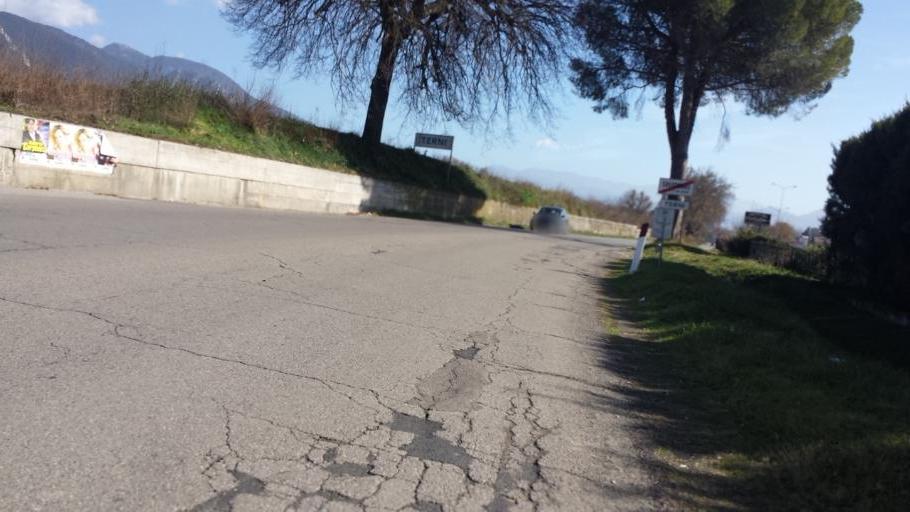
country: IT
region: Umbria
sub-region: Provincia di Terni
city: San Gemini
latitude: 42.5922
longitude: 12.5694
